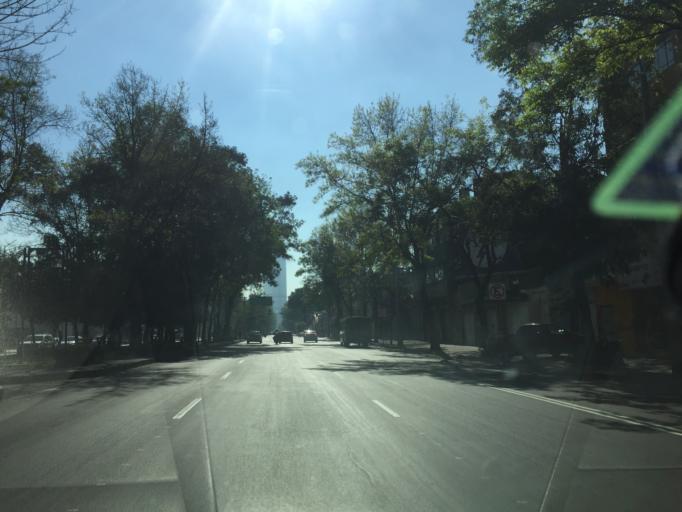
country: MX
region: Mexico City
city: Miguel Hidalgo
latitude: 19.4491
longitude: -99.1832
